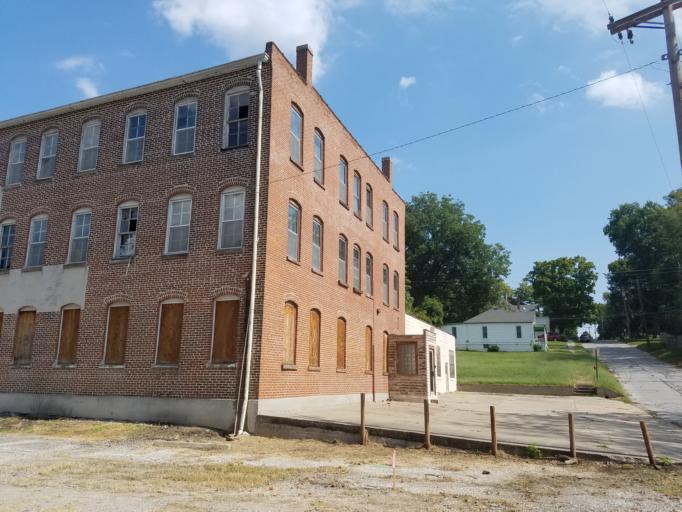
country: US
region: Missouri
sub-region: Cooper County
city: Boonville
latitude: 38.9733
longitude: -92.7421
